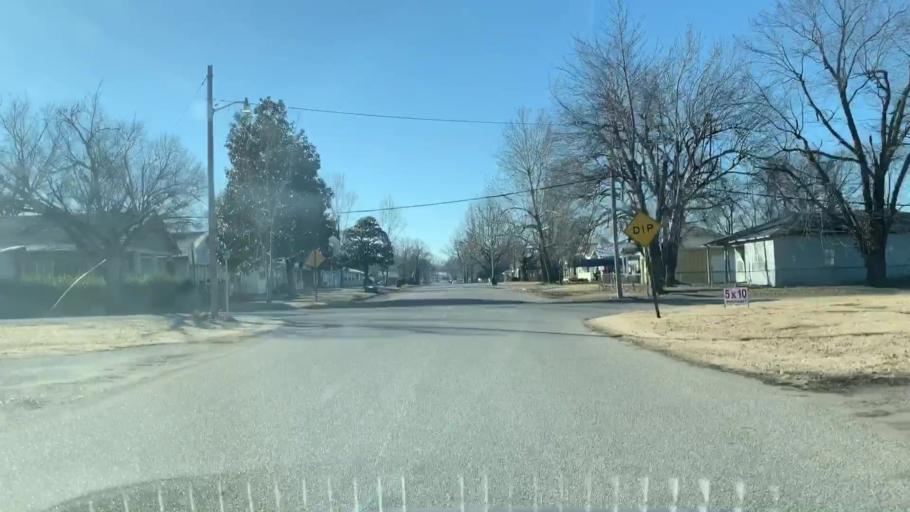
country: US
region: Kansas
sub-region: Cherokee County
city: Baxter Springs
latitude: 37.0166
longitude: -94.7346
